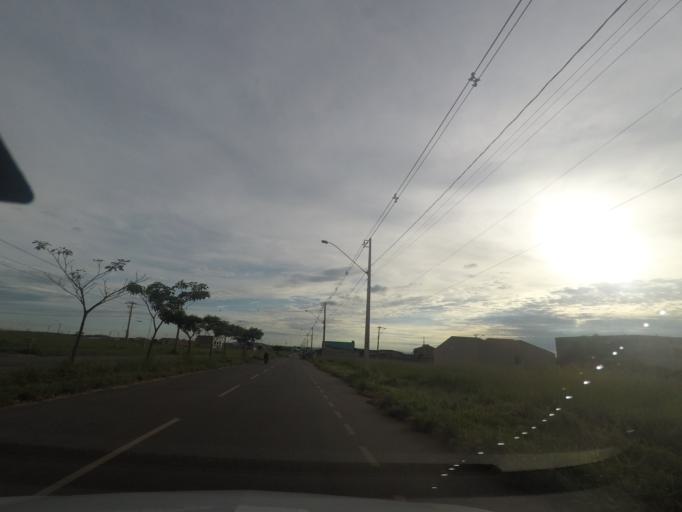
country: BR
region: Goias
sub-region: Trindade
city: Trindade
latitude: -16.7244
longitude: -49.4037
